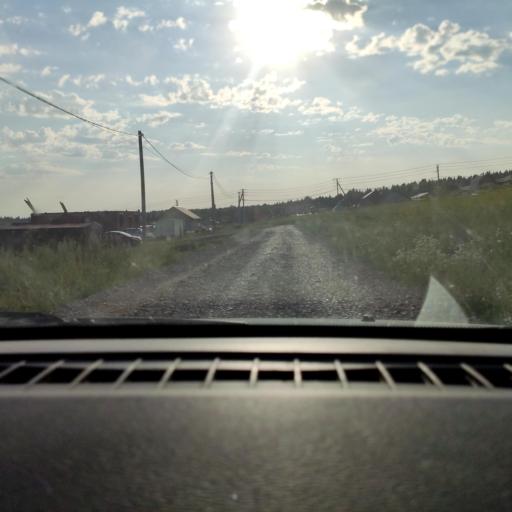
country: RU
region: Perm
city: Ferma
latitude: 57.9511
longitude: 56.3539
